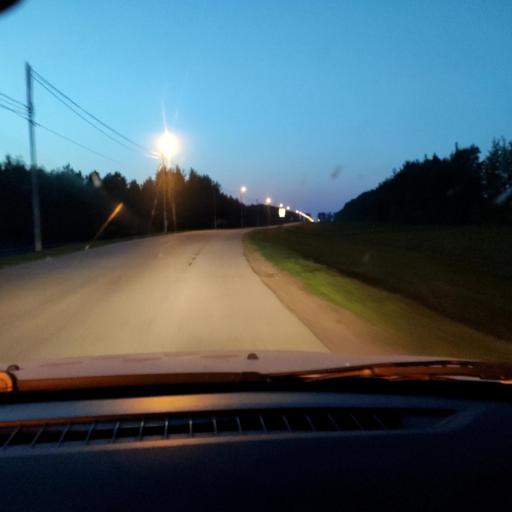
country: RU
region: Bashkortostan
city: Karmaskaly
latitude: 54.3746
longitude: 56.1512
